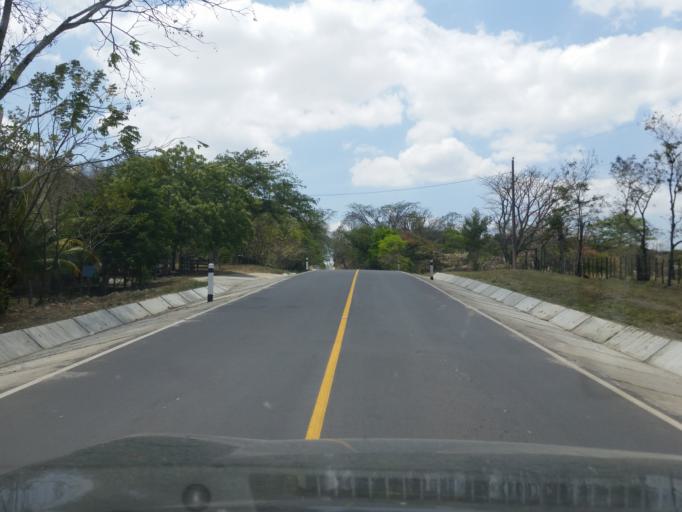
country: NI
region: Boaco
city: Boaco
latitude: 12.5153
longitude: -85.5780
